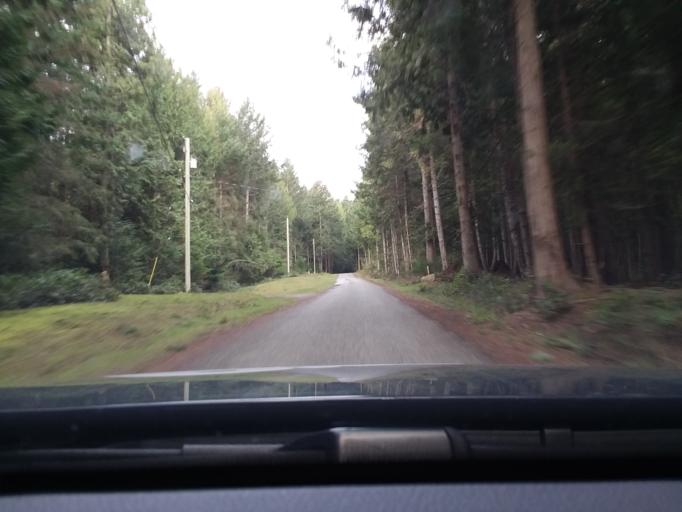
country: CA
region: British Columbia
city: North Saanich
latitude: 48.8743
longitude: -123.3286
